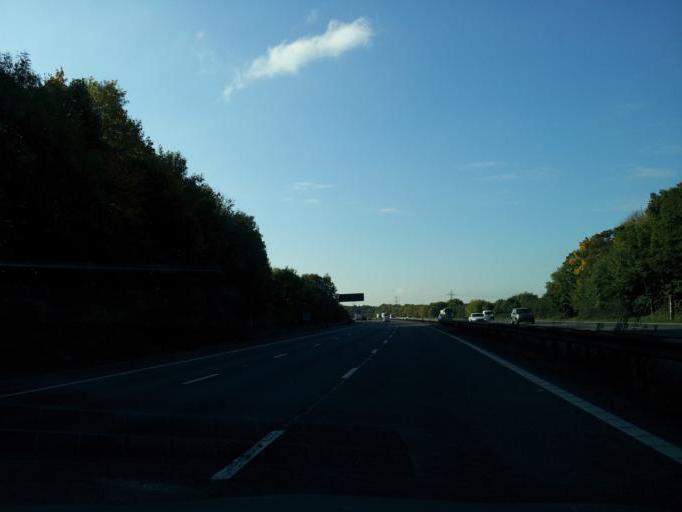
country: GB
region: England
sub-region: Leicestershire
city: Broughton Astley
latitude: 52.5044
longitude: -1.1874
